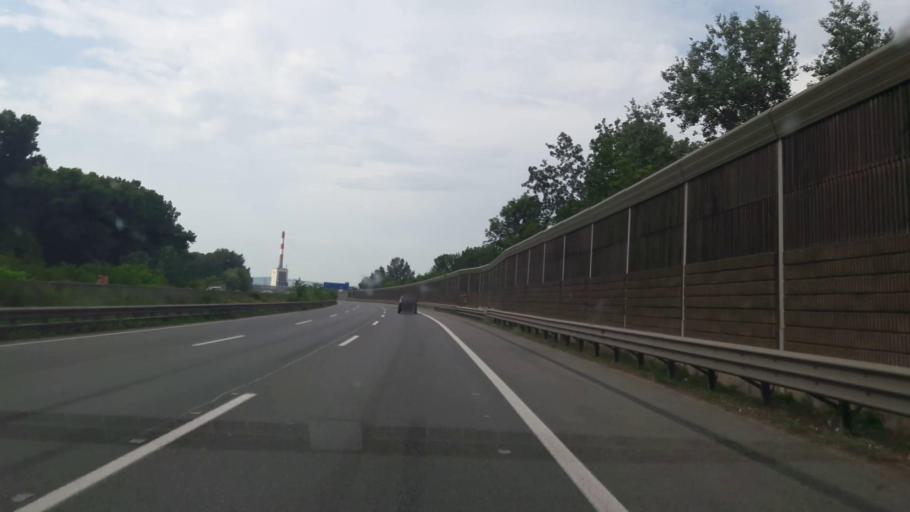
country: AT
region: Lower Austria
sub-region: Politischer Bezirk Korneuburg
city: Langenzersdorf
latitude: 48.3147
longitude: 16.3457
